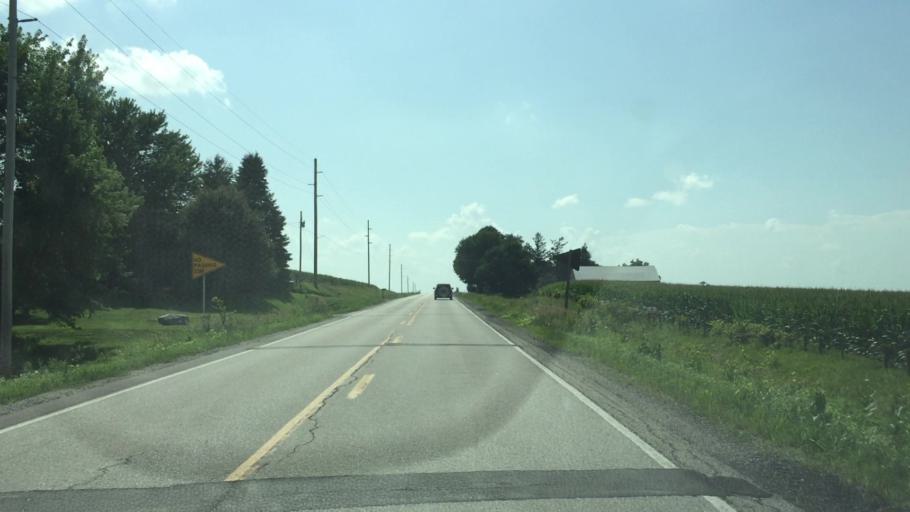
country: US
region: Iowa
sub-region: Linn County
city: Ely
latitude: 41.8474
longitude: -91.5830
